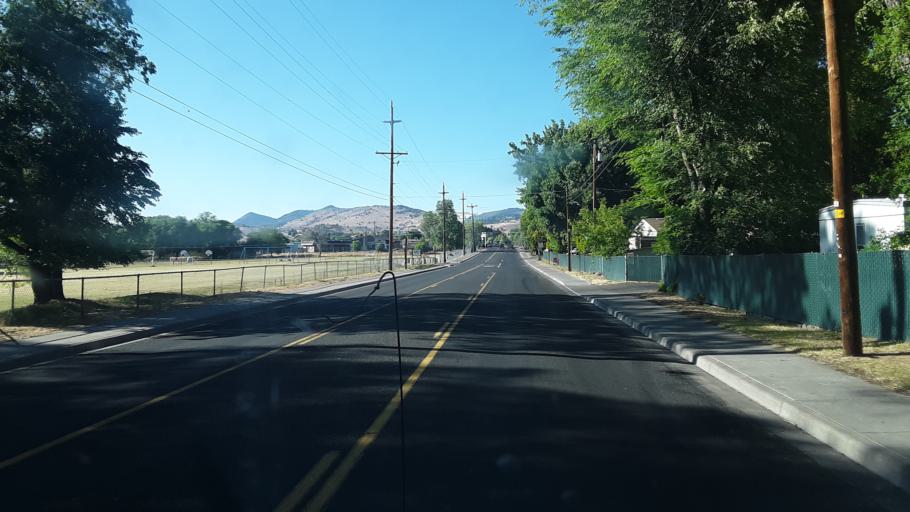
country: US
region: Oregon
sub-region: Klamath County
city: Altamont
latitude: 42.2036
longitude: -121.7378
